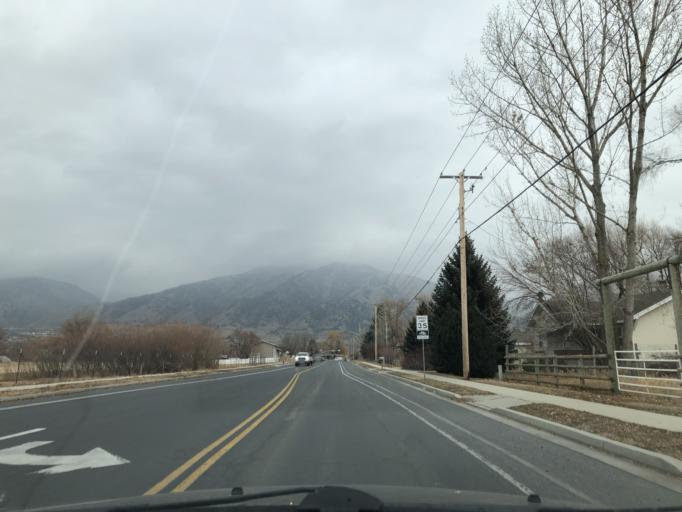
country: US
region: Utah
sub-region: Cache County
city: Nibley
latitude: 41.6747
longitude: -111.8383
